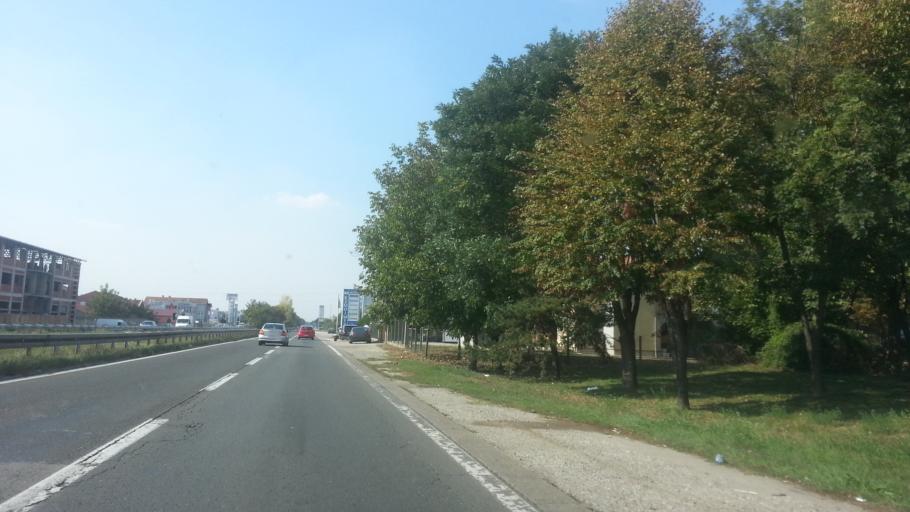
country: RS
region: Central Serbia
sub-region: Belgrade
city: Zemun
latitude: 44.8550
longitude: 20.3652
